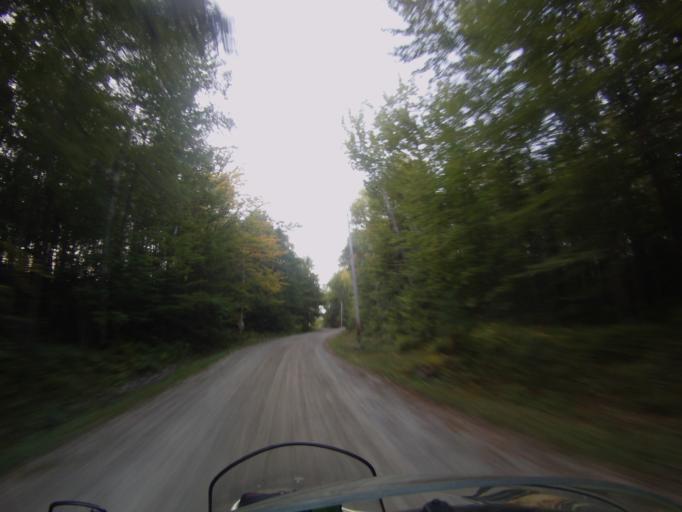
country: US
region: Vermont
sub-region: Addison County
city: Middlebury (village)
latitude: 43.9960
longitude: -73.0443
